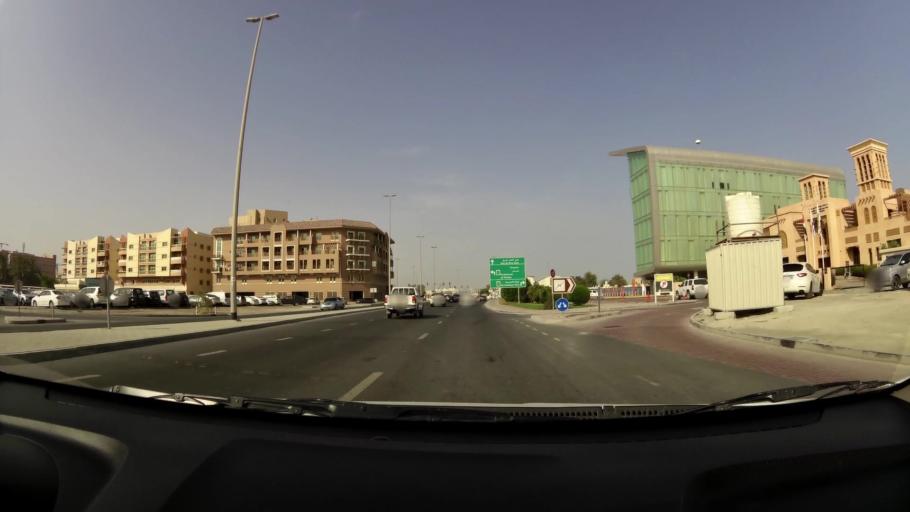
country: AE
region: Ash Shariqah
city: Sharjah
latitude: 25.2872
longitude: 55.3518
